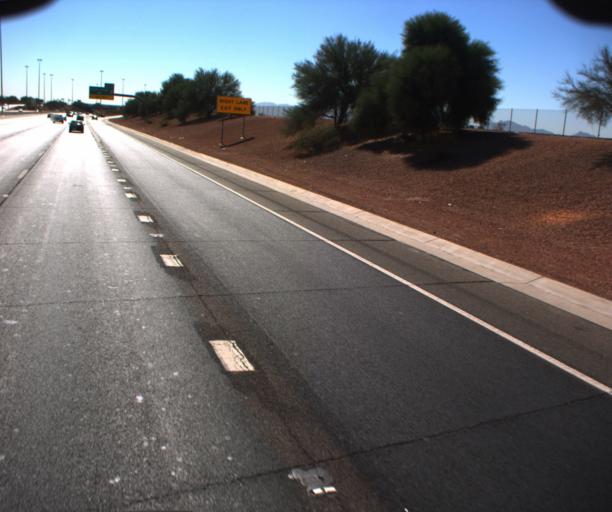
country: US
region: Arizona
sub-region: Maricopa County
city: Tolleson
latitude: 33.5001
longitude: -112.2669
